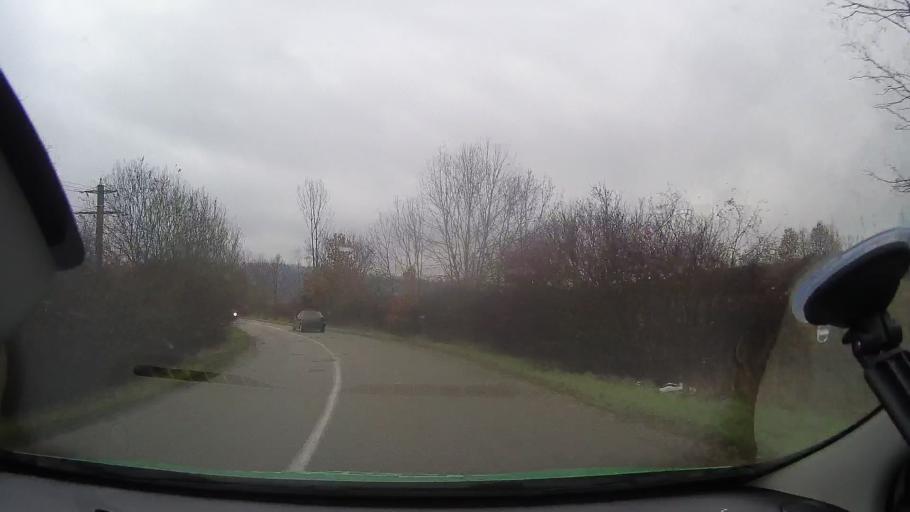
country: RO
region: Arad
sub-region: Comuna Ignesti
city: Ignesti
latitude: 46.3831
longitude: 22.1586
